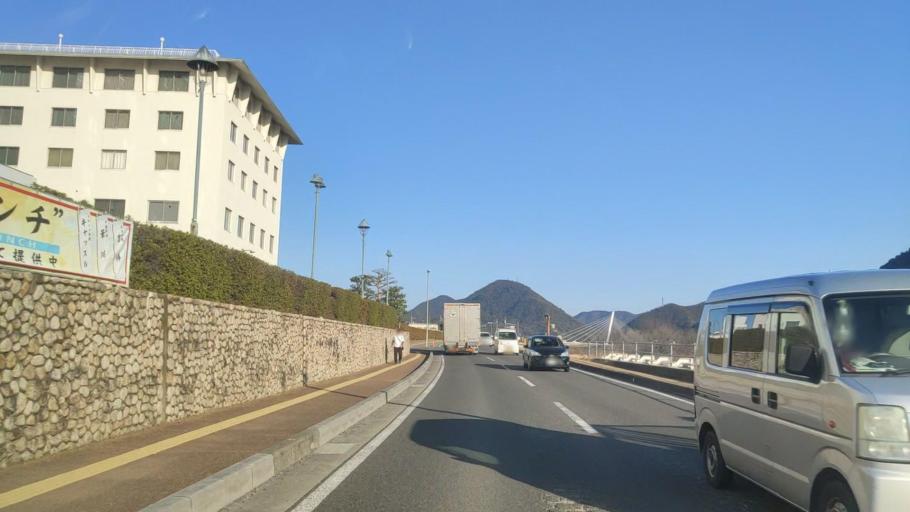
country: JP
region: Gifu
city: Gifu-shi
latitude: 35.4415
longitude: 136.7834
